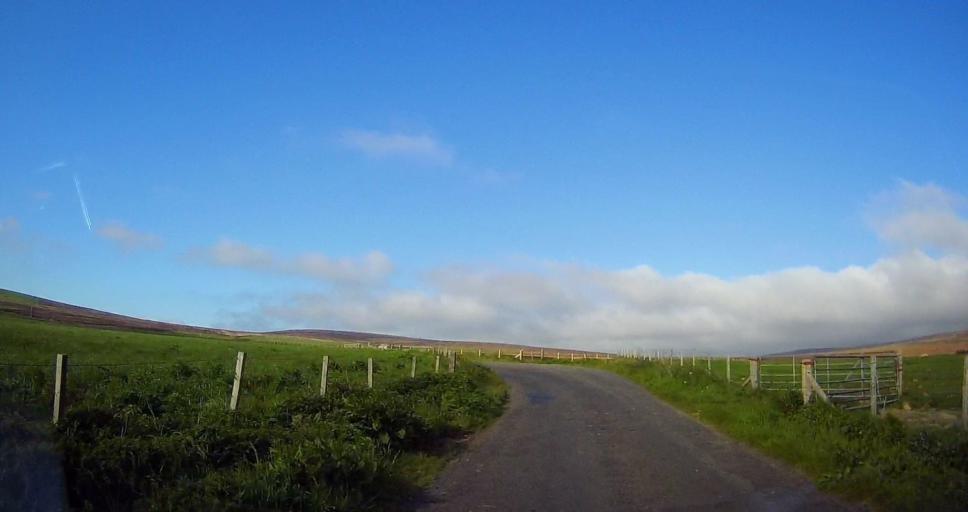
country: GB
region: Scotland
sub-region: Orkney Islands
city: Stromness
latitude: 59.0870
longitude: -3.1838
